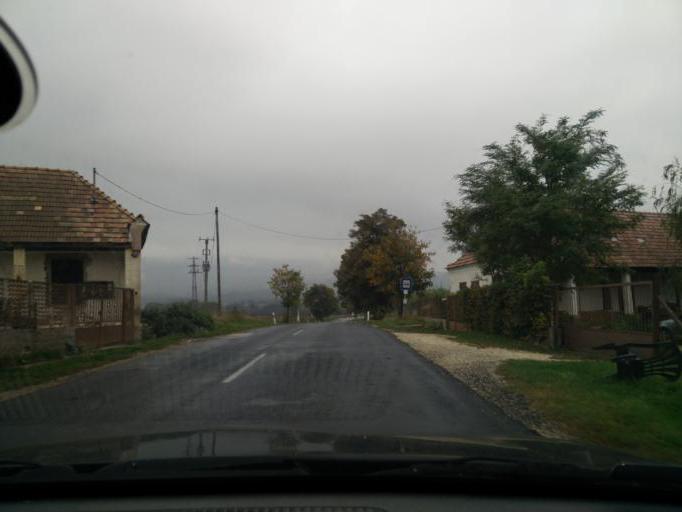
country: HU
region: Komarom-Esztergom
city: Tarjan
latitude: 47.6367
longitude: 18.5145
